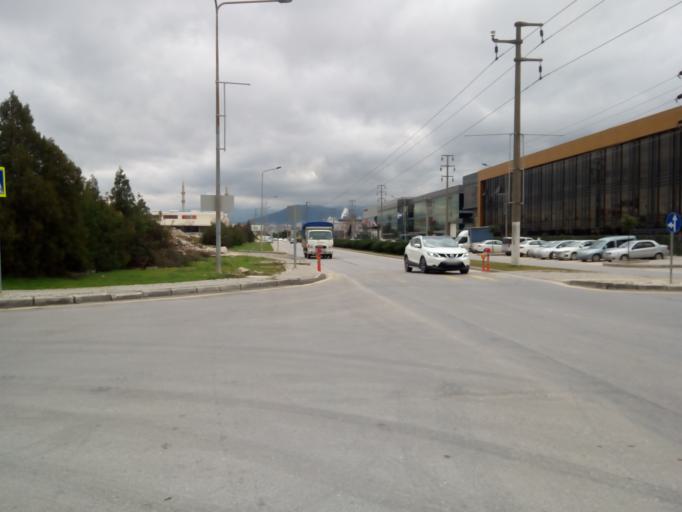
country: TR
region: Bursa
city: Niluefer
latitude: 40.2458
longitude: 28.9583
